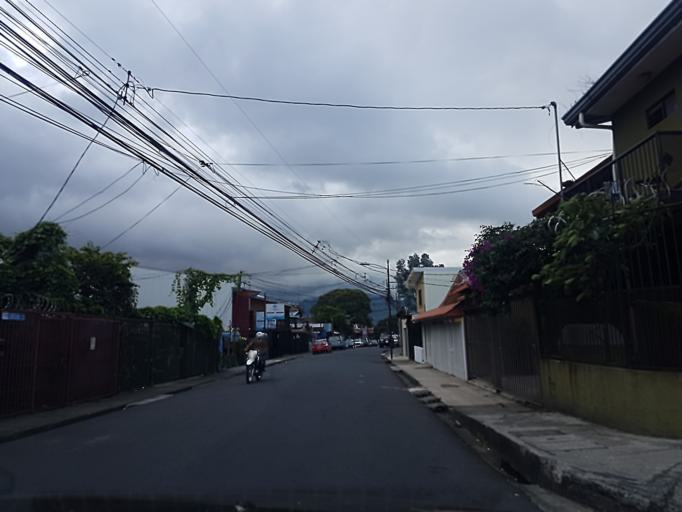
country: CR
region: San Jose
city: San Pedro
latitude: 9.9172
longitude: -84.0548
